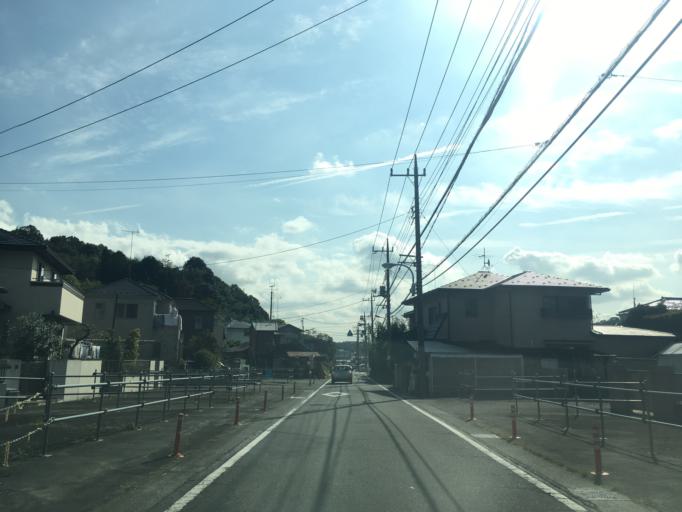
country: JP
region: Tokyo
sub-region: Machida-shi
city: Machida
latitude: 35.5959
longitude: 139.4114
